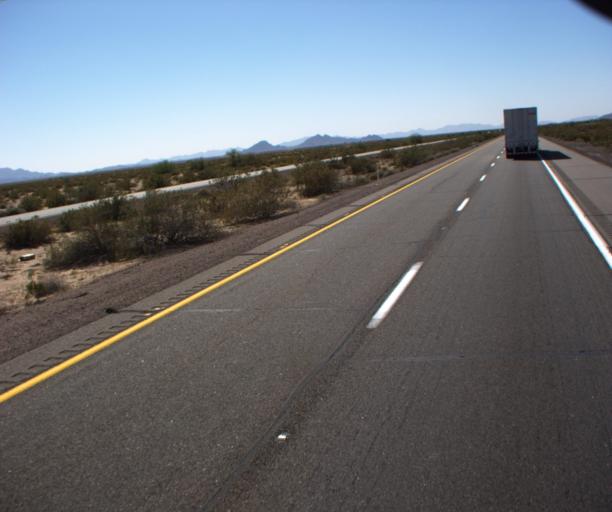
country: US
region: Arizona
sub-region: Yuma County
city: Wellton
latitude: 32.7087
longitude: -113.8547
